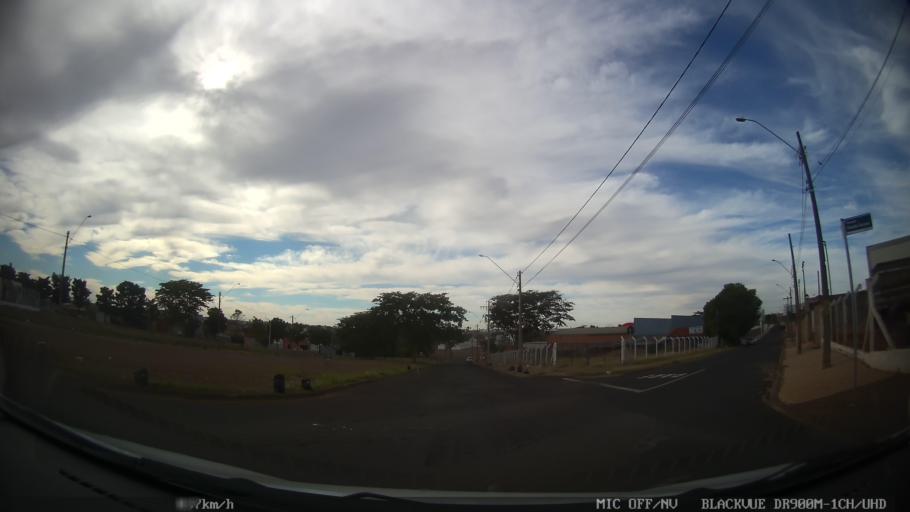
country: BR
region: Sao Paulo
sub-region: Catanduva
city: Catanduva
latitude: -21.1506
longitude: -48.9961
